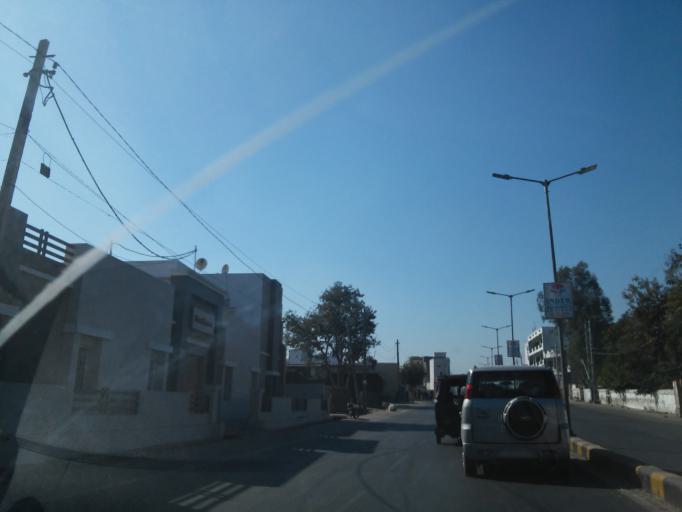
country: IN
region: Rajasthan
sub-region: Udaipur
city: Udaipur
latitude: 24.5474
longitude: 73.6877
